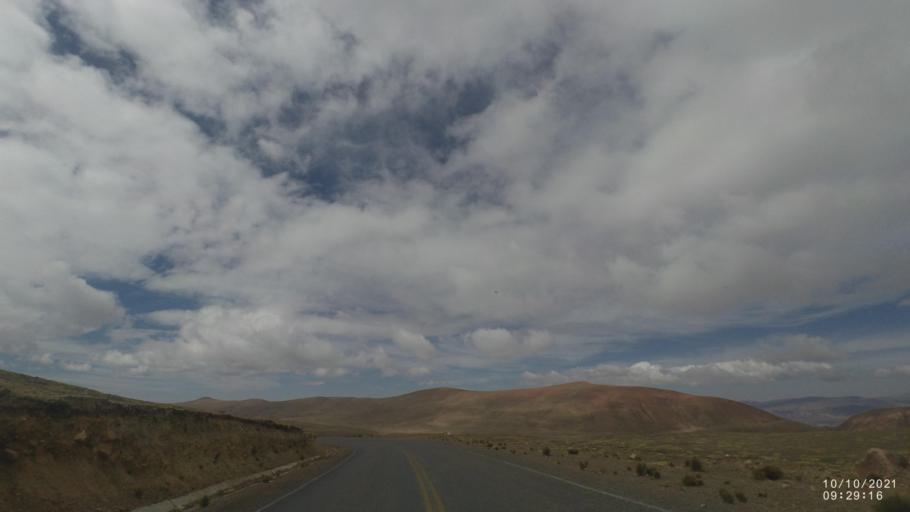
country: BO
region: La Paz
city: Quime
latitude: -17.1124
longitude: -67.3275
